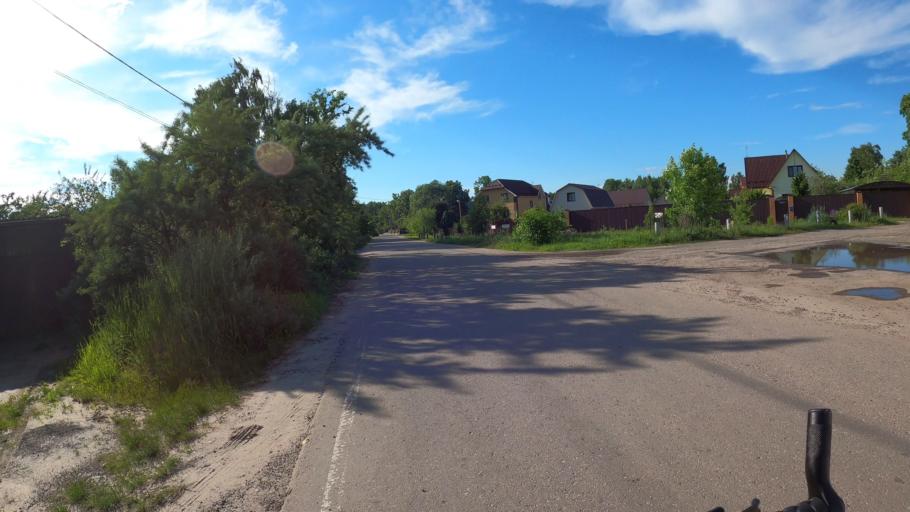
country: RU
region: Moskovskaya
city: Ashitkovo
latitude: 55.4391
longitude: 38.6042
